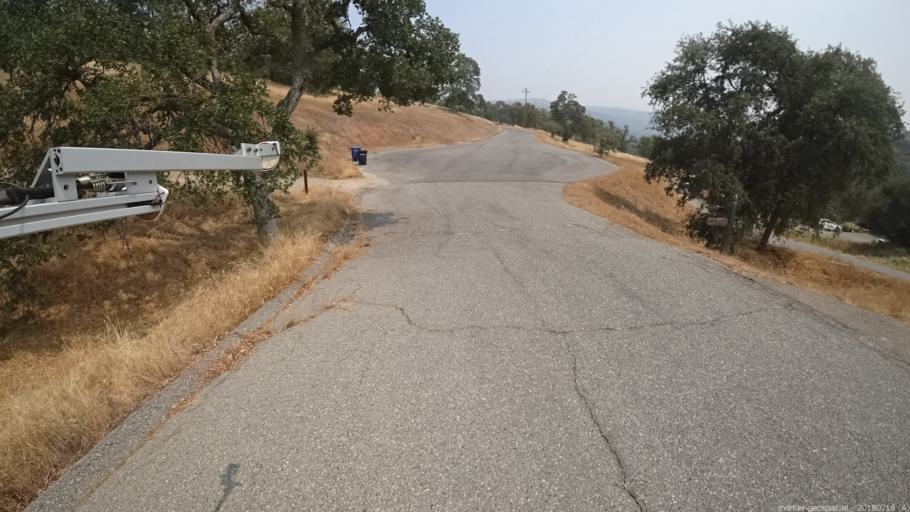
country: US
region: California
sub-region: Madera County
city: Yosemite Lakes
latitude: 37.2367
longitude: -119.7846
